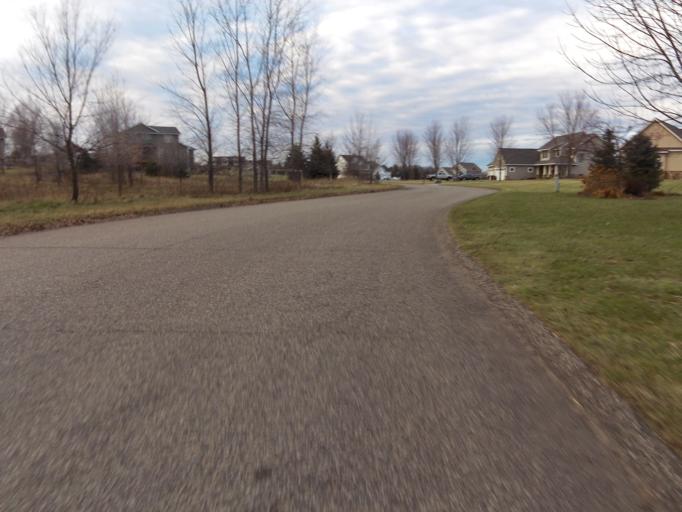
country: US
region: Minnesota
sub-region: Washington County
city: Bayport
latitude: 45.0073
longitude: -92.7993
